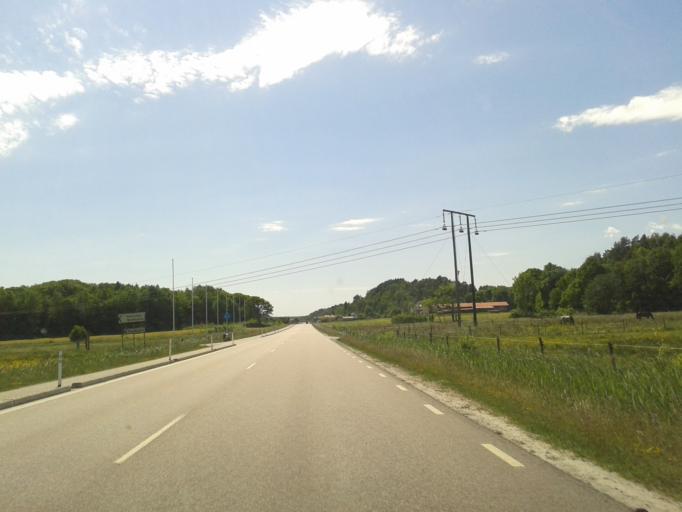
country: SE
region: Vaestra Goetaland
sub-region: Stenungsunds Kommun
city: Stora Hoga
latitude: 58.0348
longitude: 11.8800
